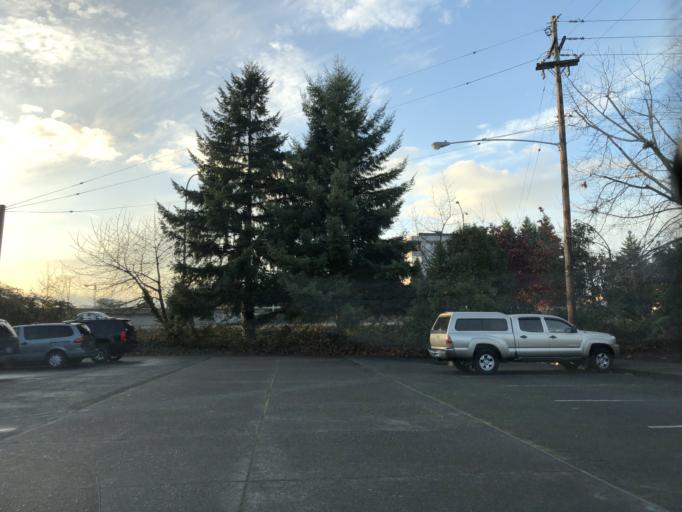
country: US
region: Washington
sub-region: Clark County
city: Vancouver
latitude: 45.6248
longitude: -122.6683
